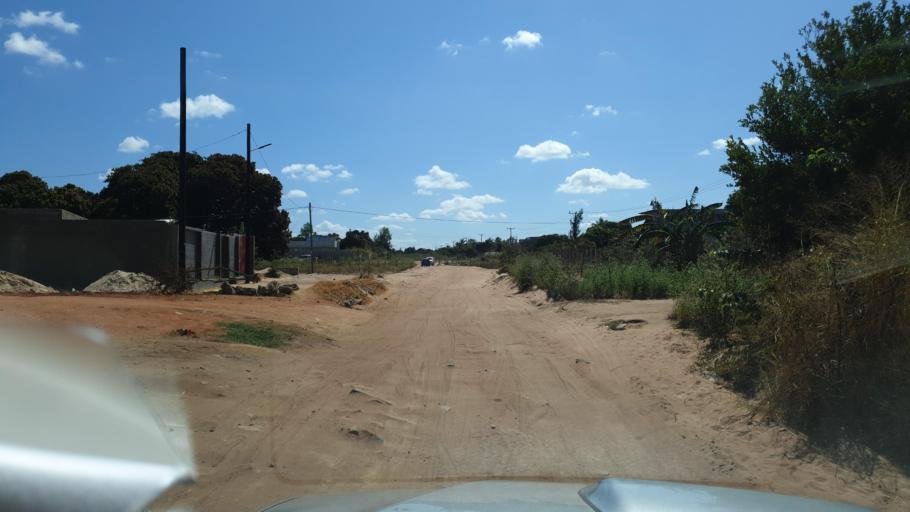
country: MZ
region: Nampula
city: Nampula
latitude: -15.1083
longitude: 39.2062
